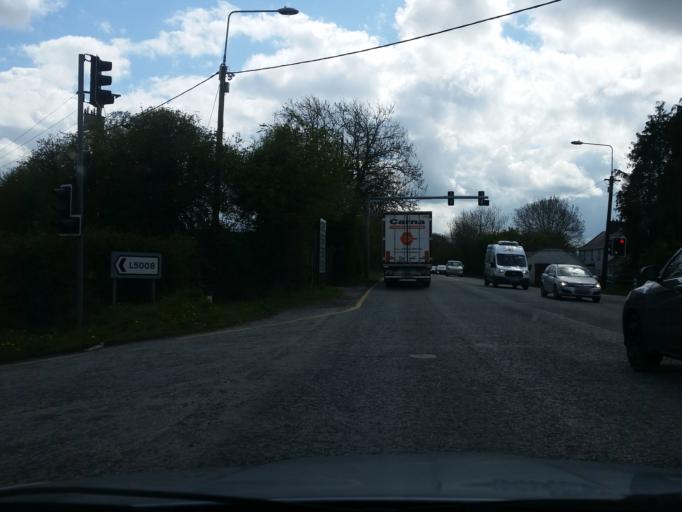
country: IE
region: Leinster
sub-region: An Mhi
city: Ratoath
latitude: 53.5588
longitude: -6.4404
